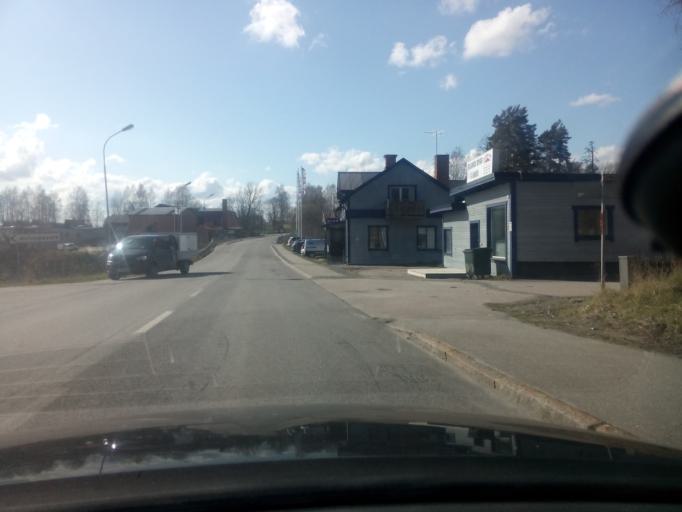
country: SE
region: Soedermanland
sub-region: Flens Kommun
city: Malmkoping
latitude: 59.1301
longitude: 16.7388
